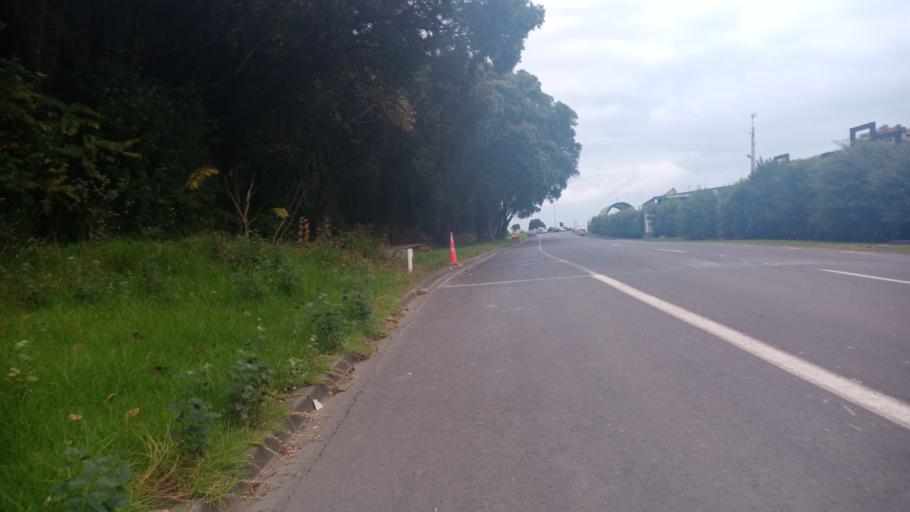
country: NZ
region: Gisborne
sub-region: Gisborne District
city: Gisborne
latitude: -38.6780
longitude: 178.0268
